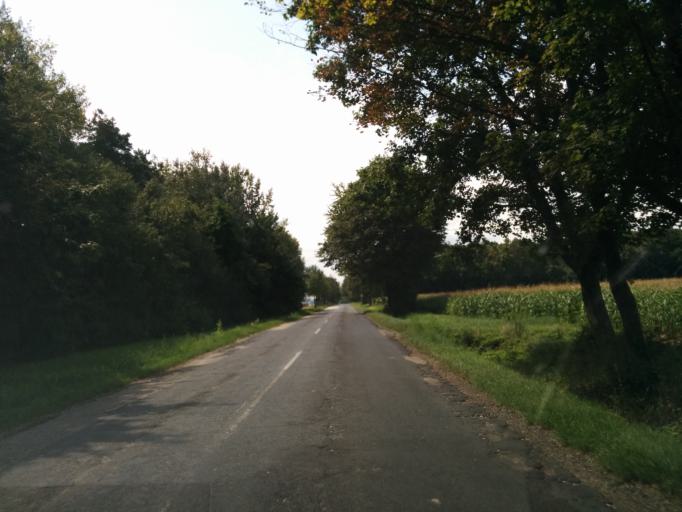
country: HU
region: Vas
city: Csepreg
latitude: 47.4693
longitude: 16.7214
